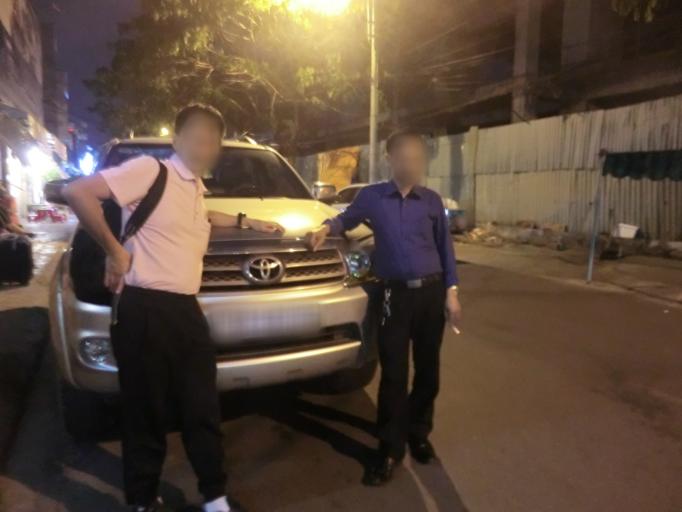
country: VN
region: Da Nang
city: Da Nang
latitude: 16.0674
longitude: 108.2218
